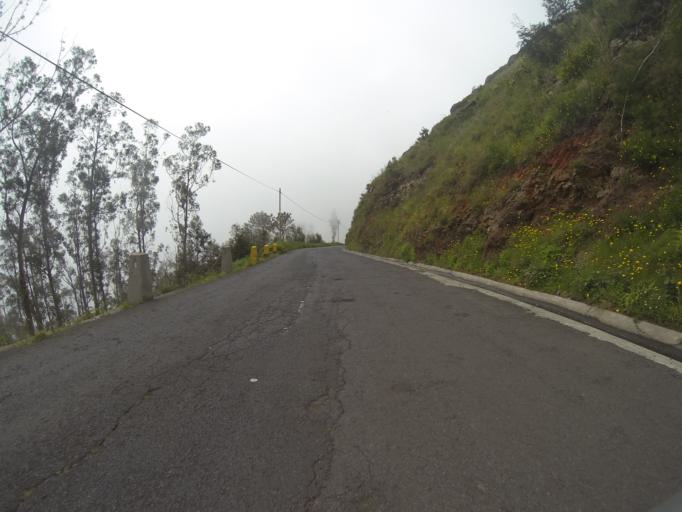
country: PT
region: Madeira
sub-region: Funchal
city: Nossa Senhora do Monte
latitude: 32.6897
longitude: -16.9018
